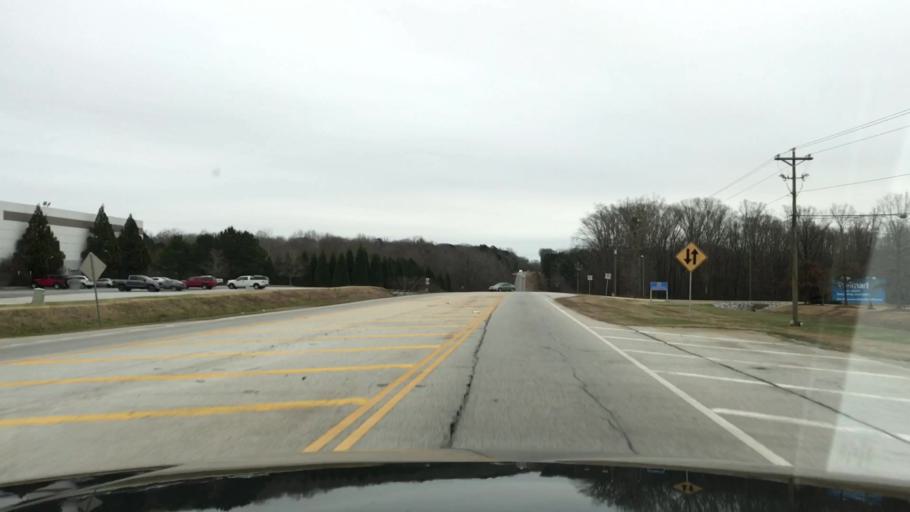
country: US
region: Georgia
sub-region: Walton County
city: Monroe
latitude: 33.8075
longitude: -83.6758
